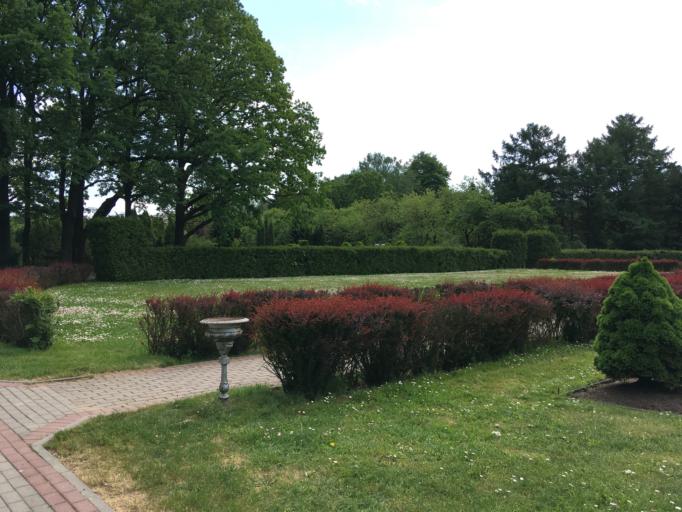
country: BY
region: Minsk
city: Minsk
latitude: 53.9166
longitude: 27.6126
